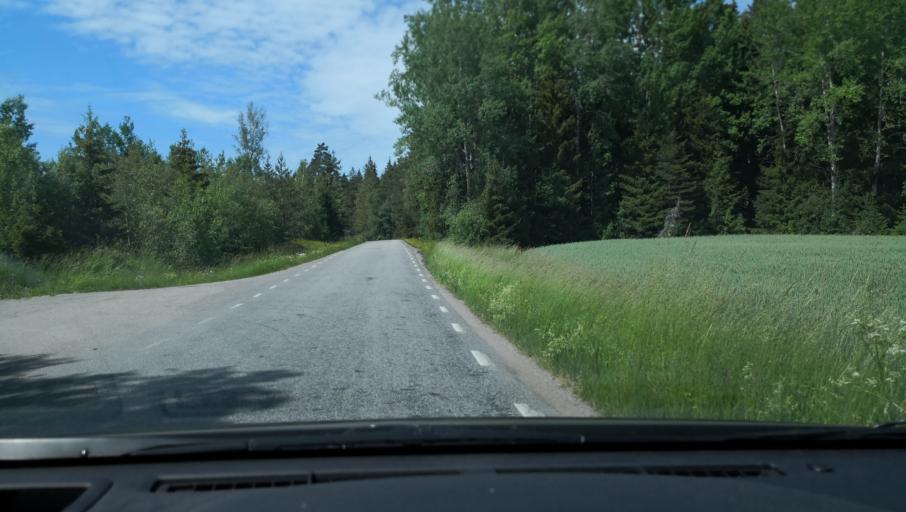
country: SE
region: Stockholm
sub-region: Sigtuna Kommun
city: Sigtuna
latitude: 59.6882
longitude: 17.6670
